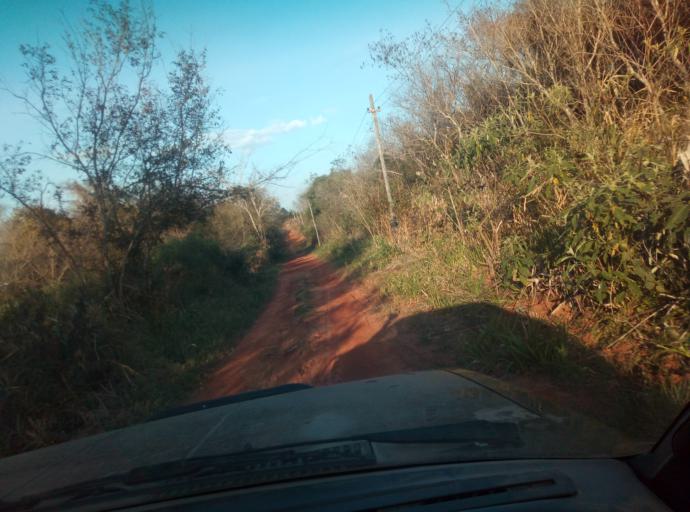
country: PY
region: Caaguazu
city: Doctor Cecilio Baez
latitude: -25.1532
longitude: -56.2384
